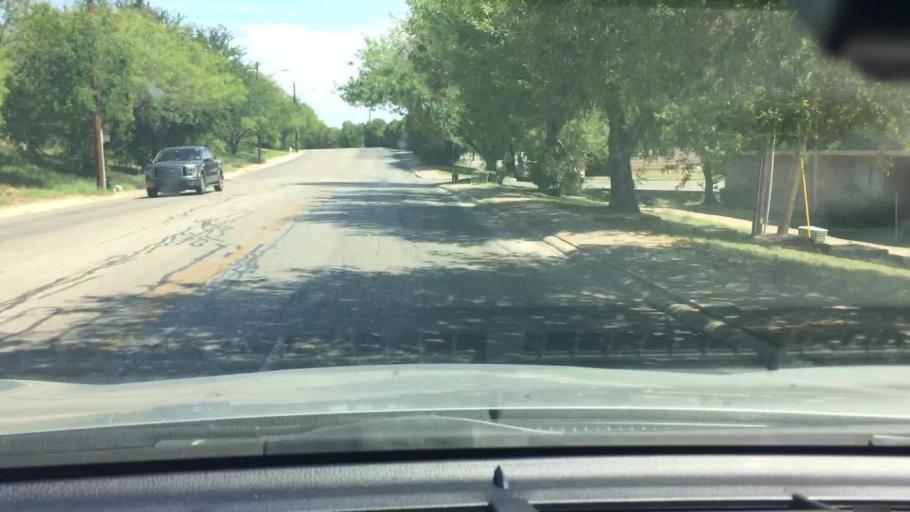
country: US
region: Texas
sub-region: Bexar County
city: San Antonio
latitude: 29.3804
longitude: -98.4311
